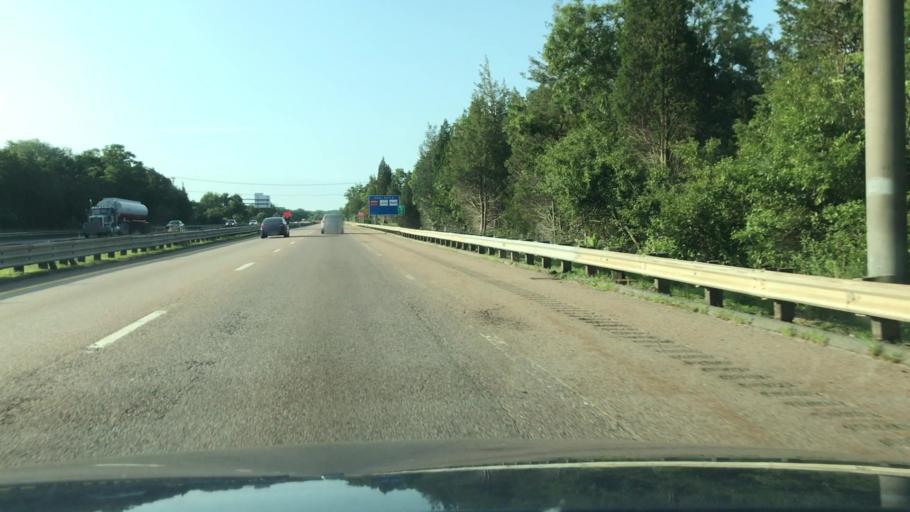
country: US
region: Massachusetts
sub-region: Plymouth County
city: Kingston
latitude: 41.9999
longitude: -70.7225
